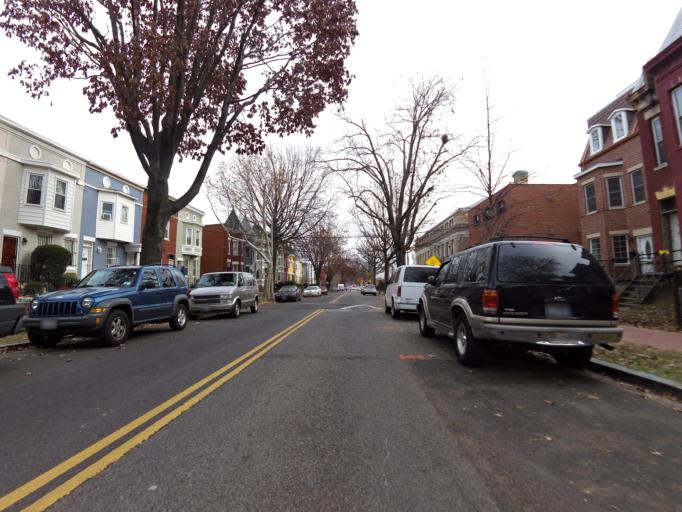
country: US
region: Washington, D.C.
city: Washington, D.C.
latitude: 38.9096
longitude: -77.0142
